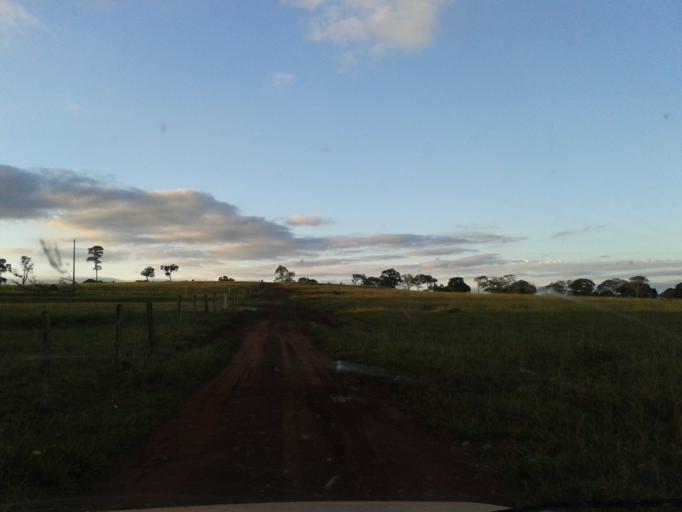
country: BR
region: Minas Gerais
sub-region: Campina Verde
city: Campina Verde
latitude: -19.4972
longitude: -49.6793
